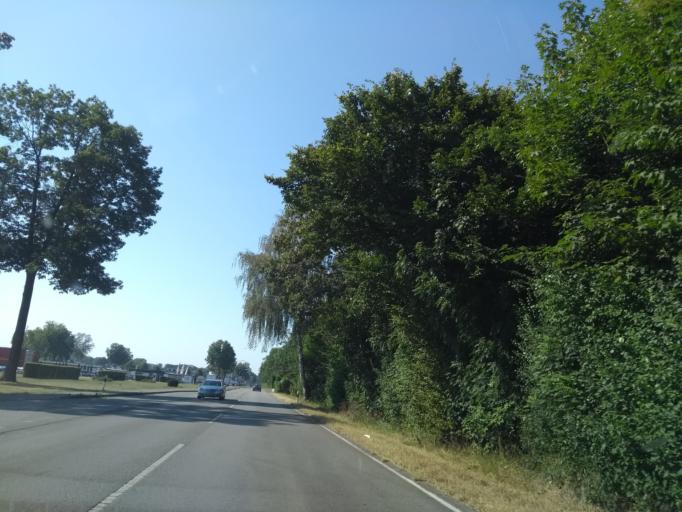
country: DE
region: North Rhine-Westphalia
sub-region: Regierungsbezirk Arnsberg
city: Lippstadt
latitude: 51.7160
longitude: 8.3691
